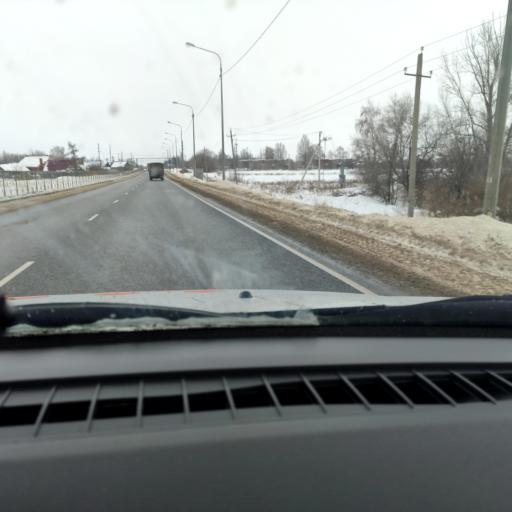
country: RU
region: Samara
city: Dubovyy Umet
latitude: 52.9633
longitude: 50.2882
